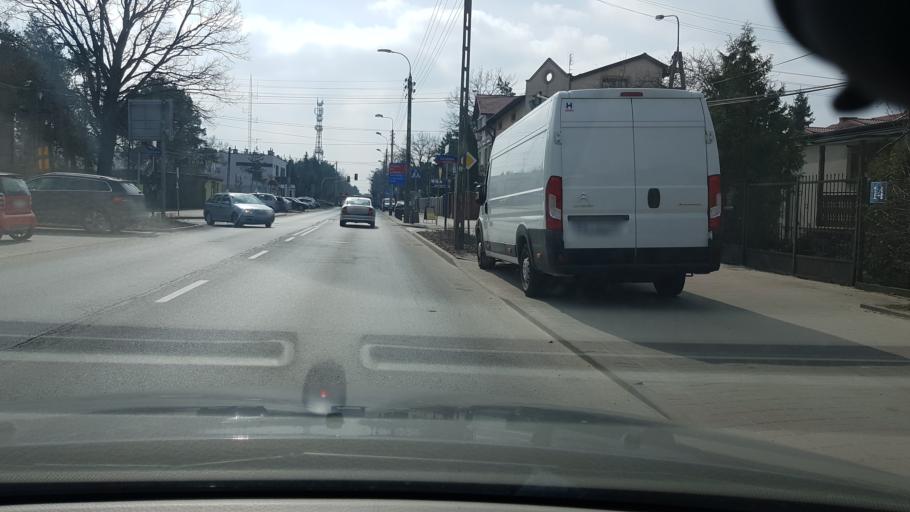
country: PL
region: Masovian Voivodeship
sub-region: Warszawa
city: Wesola
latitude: 52.2521
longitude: 21.2240
